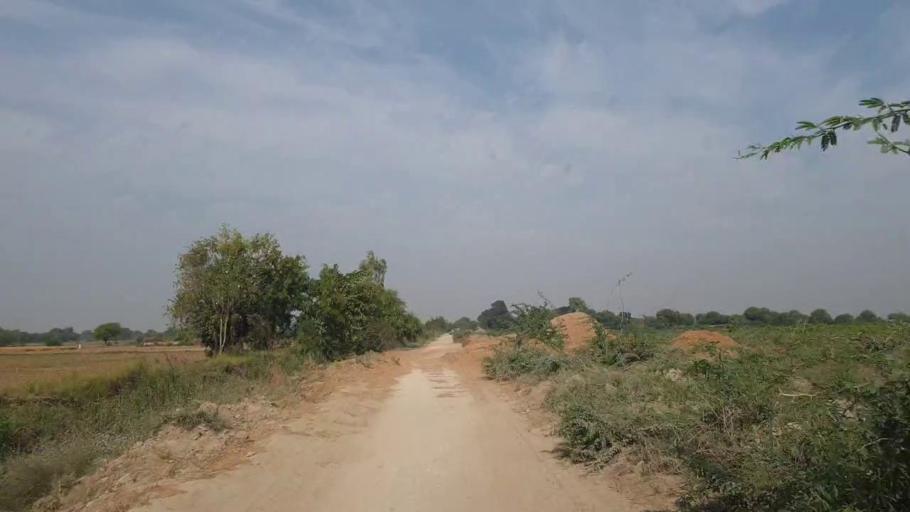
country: PK
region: Sindh
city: Tando Bago
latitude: 24.8900
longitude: 69.0016
